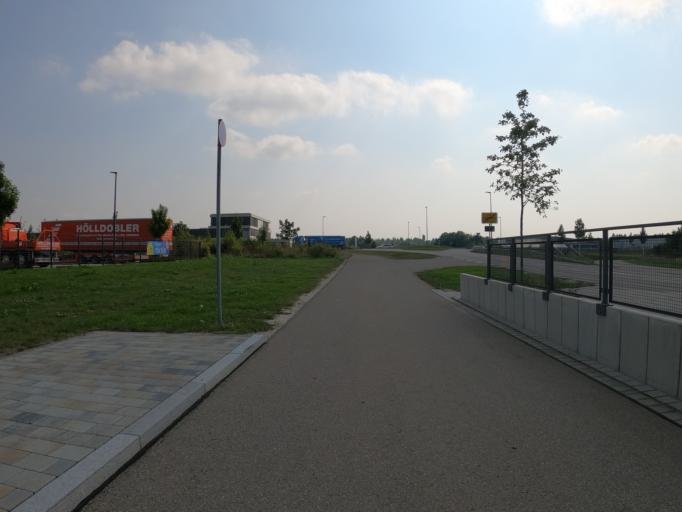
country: DE
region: Bavaria
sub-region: Swabia
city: Bubesheim
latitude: 48.4418
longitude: 10.2368
